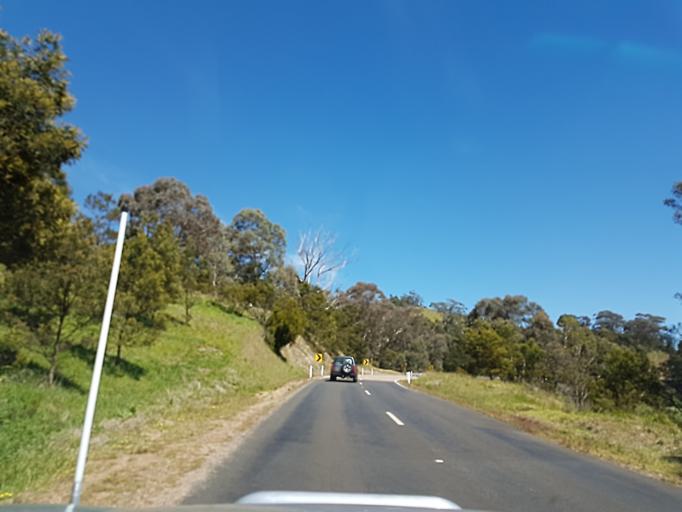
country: AU
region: Victoria
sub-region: Alpine
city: Mount Beauty
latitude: -37.1662
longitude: 147.6692
